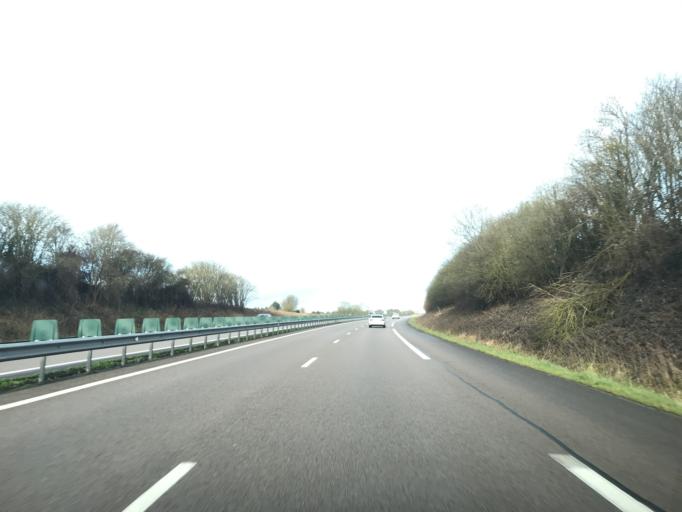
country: FR
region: Haute-Normandie
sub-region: Departement de l'Eure
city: Beuzeville
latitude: 49.3326
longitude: 0.3911
